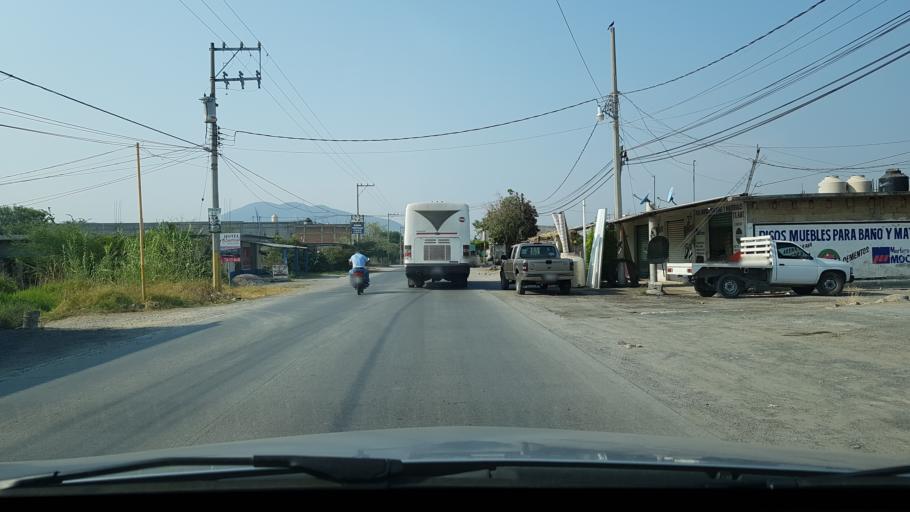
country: MX
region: Morelos
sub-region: Tlaquiltenango
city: Alfredo V. Bonfil (Chacampalco)
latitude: 18.6499
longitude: -99.1556
